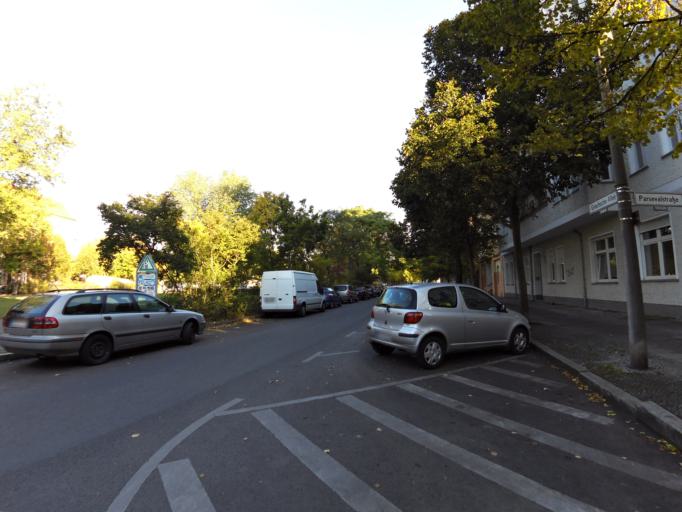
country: DE
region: Berlin
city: Oberschoneweide
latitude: 52.4643
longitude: 13.5166
